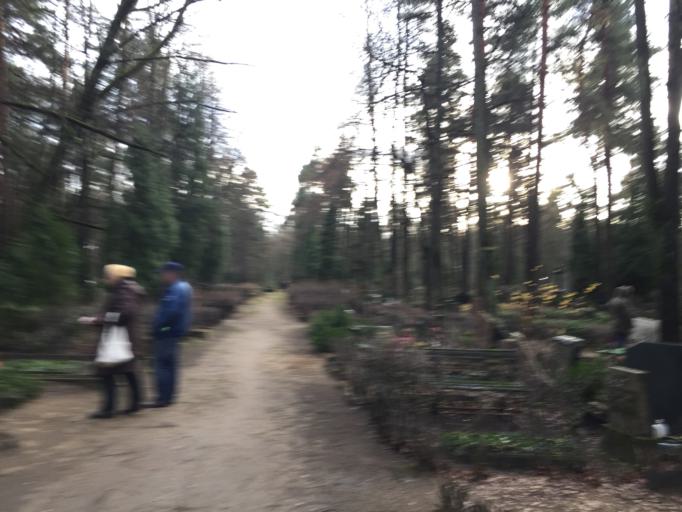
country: LV
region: Riga
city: Jaunciems
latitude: 56.9961
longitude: 24.1386
